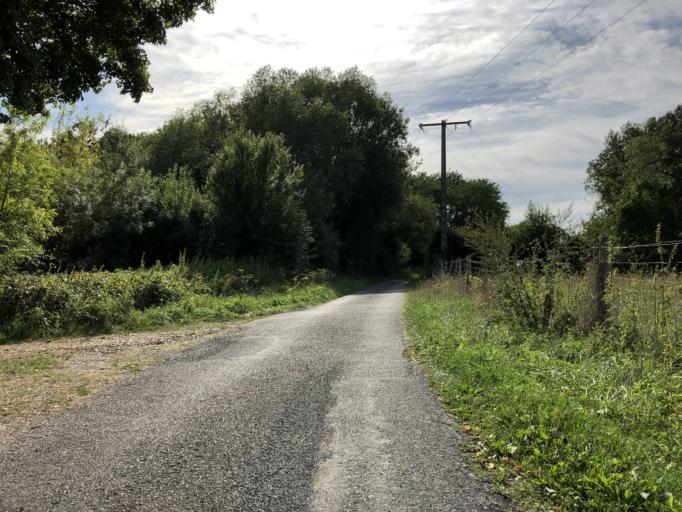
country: FR
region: Pays de la Loire
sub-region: Departement de la Sarthe
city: Chateau-du-Loir
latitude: 47.6815
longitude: 0.4316
